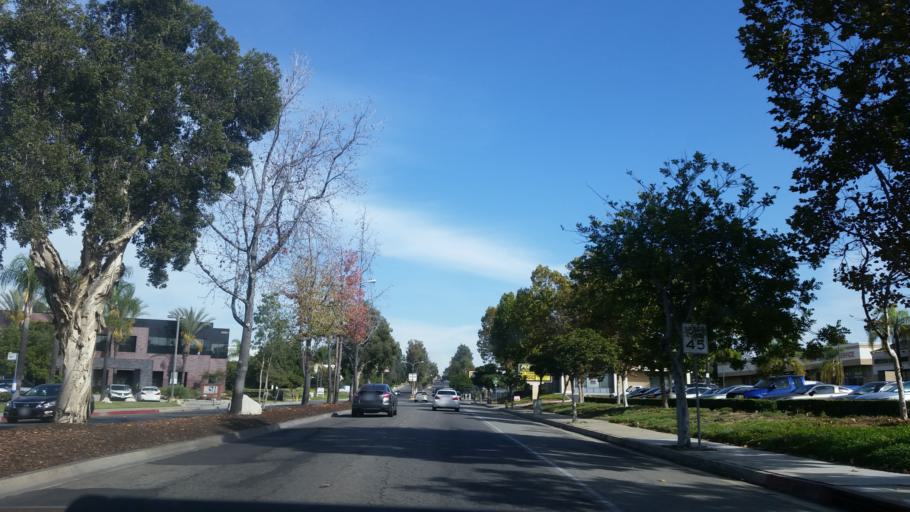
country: US
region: California
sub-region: Los Angeles County
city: San Dimas
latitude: 34.1283
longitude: -117.8283
